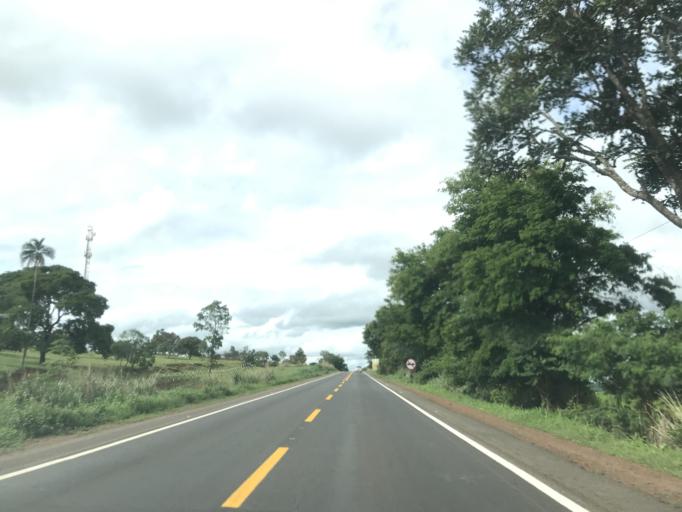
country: BR
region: Goias
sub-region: Piracanjuba
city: Piracanjuba
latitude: -17.2206
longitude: -48.7116
